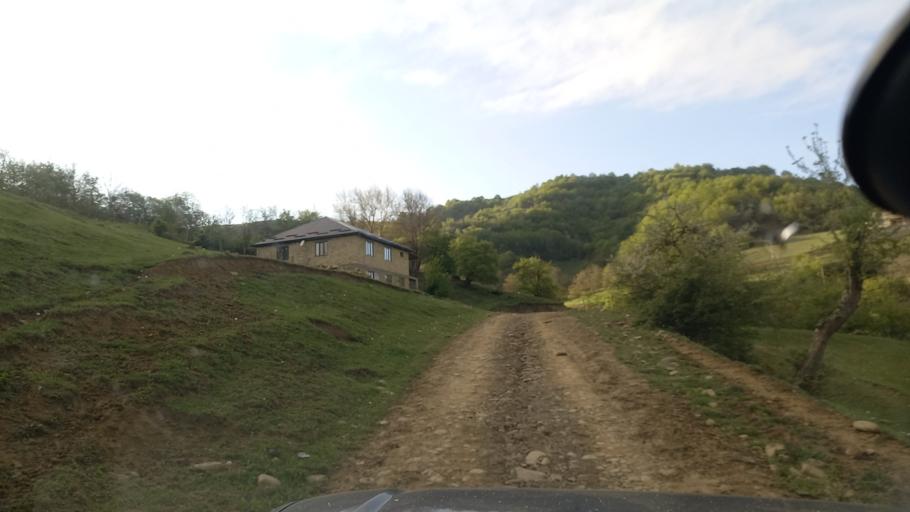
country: RU
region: Dagestan
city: Khuchni
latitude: 41.9464
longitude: 47.8346
